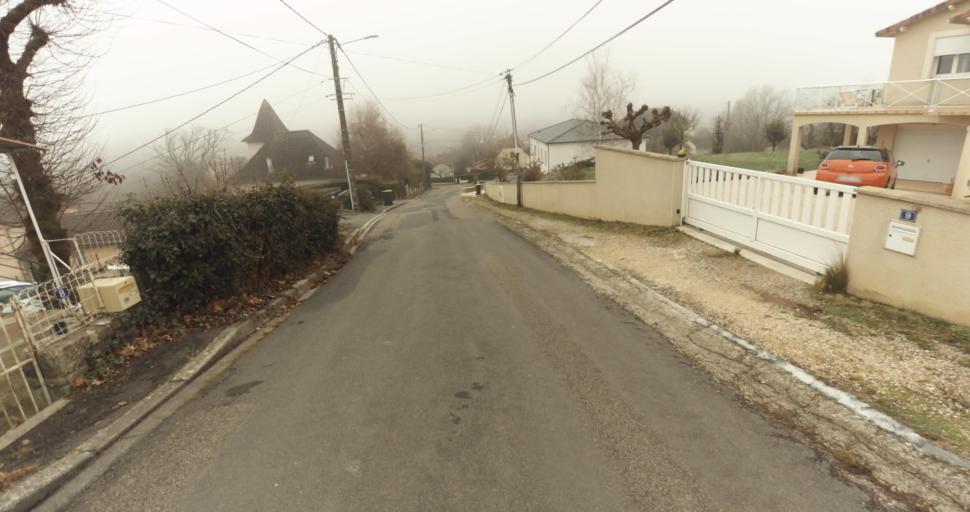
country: FR
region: Midi-Pyrenees
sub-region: Departement du Lot
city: Figeac
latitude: 44.6157
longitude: 2.0447
